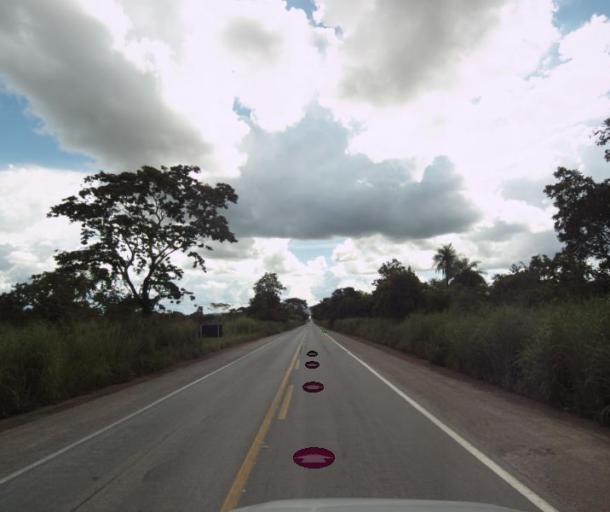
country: BR
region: Goias
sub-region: Porangatu
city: Porangatu
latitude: -13.5550
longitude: -49.0740
